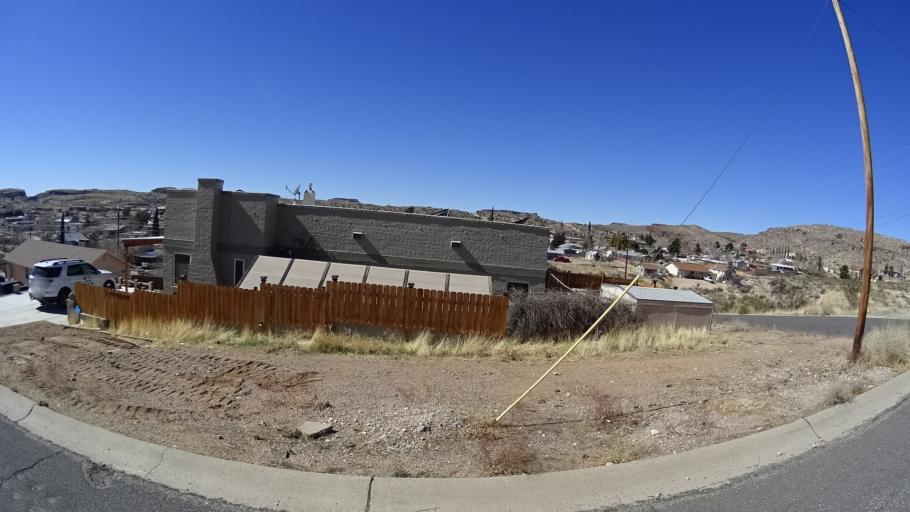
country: US
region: Arizona
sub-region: Mohave County
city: Kingman
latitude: 35.1963
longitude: -114.0587
